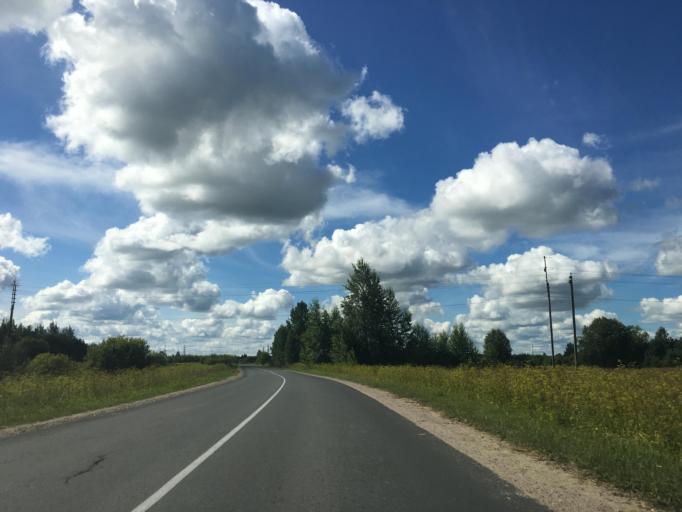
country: RU
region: Pskov
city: Pskov
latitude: 57.7744
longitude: 28.1631
